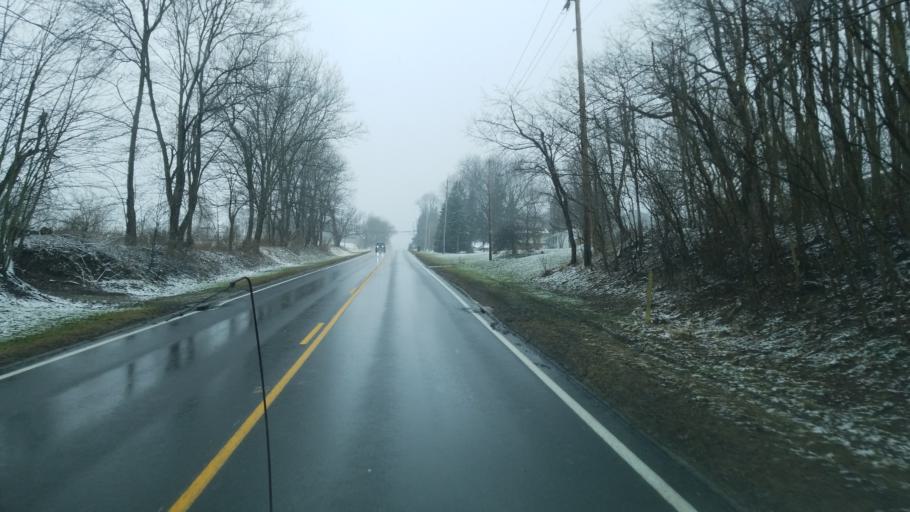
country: US
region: Ohio
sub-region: Portage County
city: Mantua
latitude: 41.3105
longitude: -81.2002
